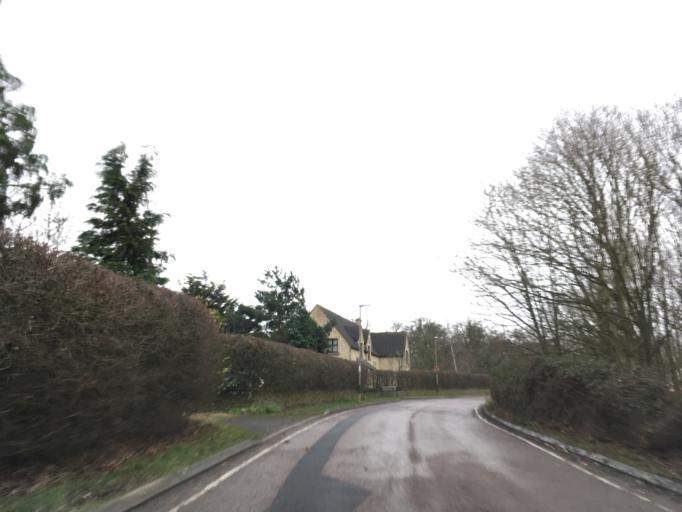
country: GB
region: England
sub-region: Gloucestershire
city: Cheltenham
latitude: 51.8740
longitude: -2.0924
